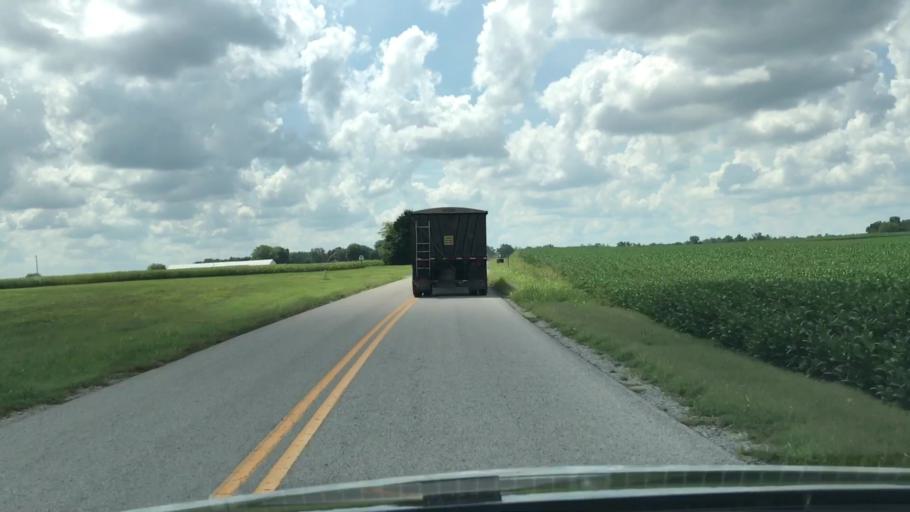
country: US
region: Kentucky
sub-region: Todd County
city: Guthrie
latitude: 36.6778
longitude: -87.0225
